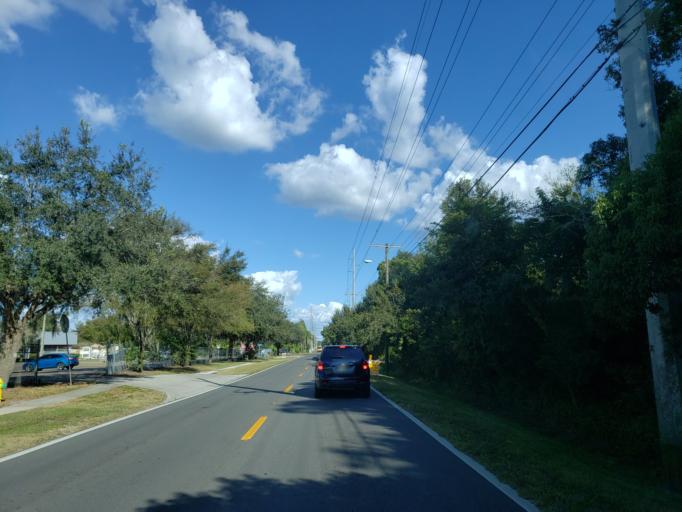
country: US
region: Florida
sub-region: Hillsborough County
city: Plant City
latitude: 28.0037
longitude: -82.1353
